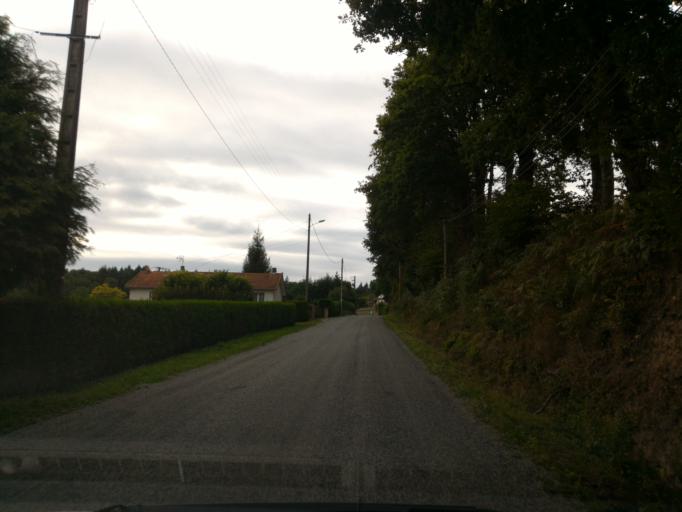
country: FR
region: Limousin
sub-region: Departement de la Haute-Vienne
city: Saint-Junien
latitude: 45.8977
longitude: 0.8756
